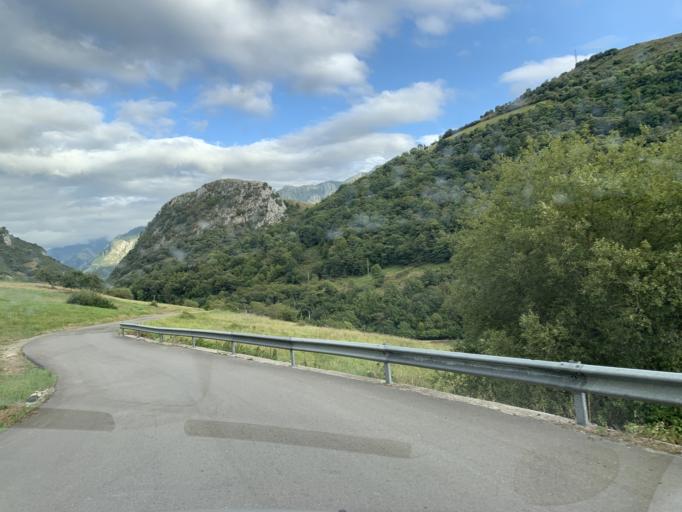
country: ES
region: Asturias
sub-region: Province of Asturias
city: Carrena
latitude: 43.3176
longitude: -4.8545
